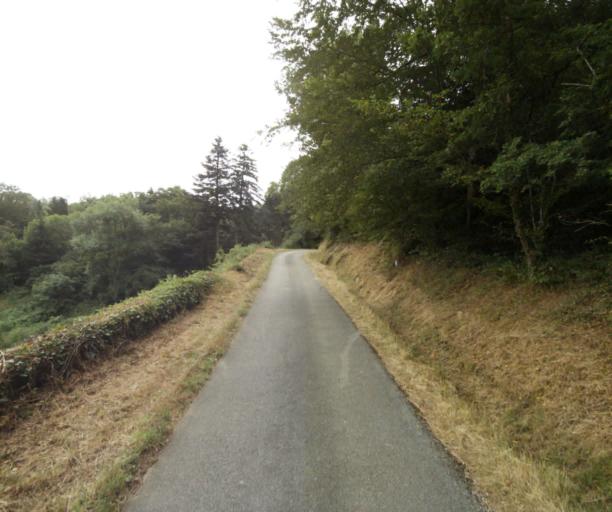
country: FR
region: Midi-Pyrenees
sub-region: Departement du Tarn
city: Soreze
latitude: 43.4162
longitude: 2.0867
